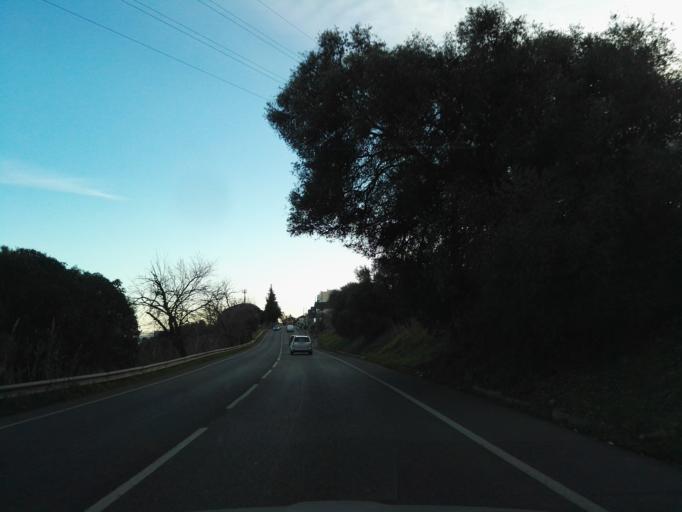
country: PT
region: Lisbon
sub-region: Vila Franca de Xira
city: Vialonga
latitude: 38.8810
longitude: -9.0507
